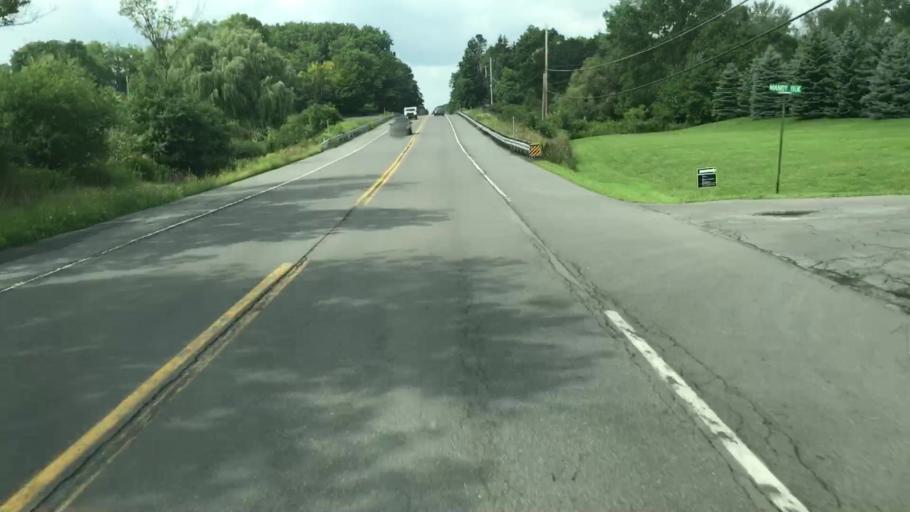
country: US
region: New York
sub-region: Onondaga County
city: Skaneateles
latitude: 42.9417
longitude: -76.4796
